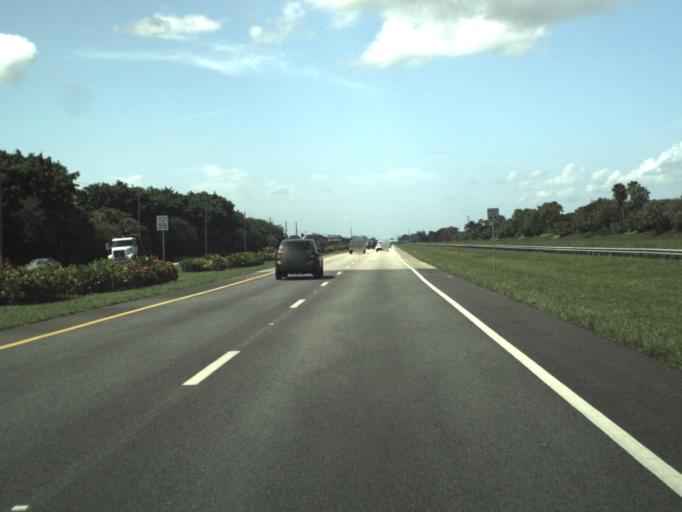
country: US
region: Florida
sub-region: Palm Beach County
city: Villages of Oriole
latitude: 26.4384
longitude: -80.2043
